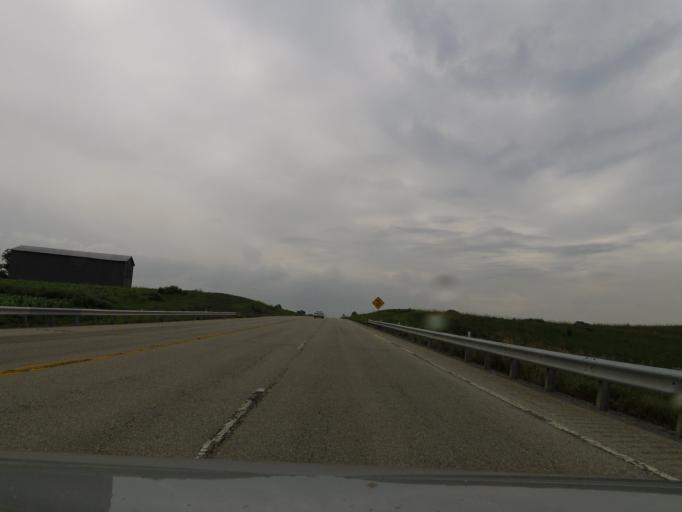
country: US
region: Kentucky
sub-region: Mason County
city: Maysville
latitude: 38.5553
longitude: -83.8226
